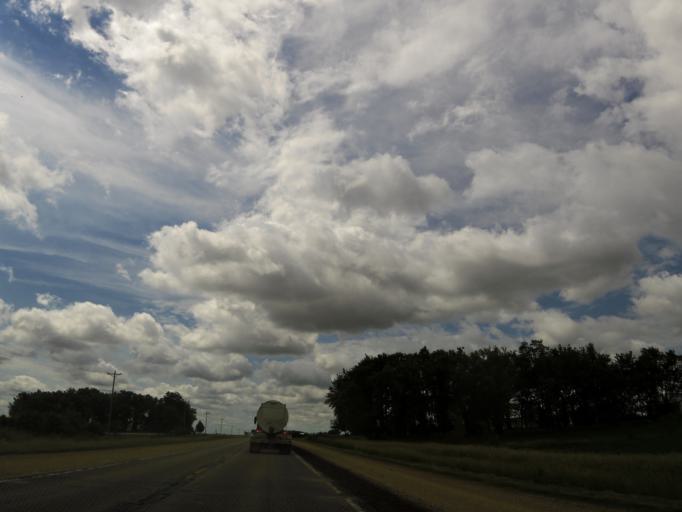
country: US
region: Iowa
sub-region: Howard County
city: Cresco
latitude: 43.3112
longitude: -92.2989
